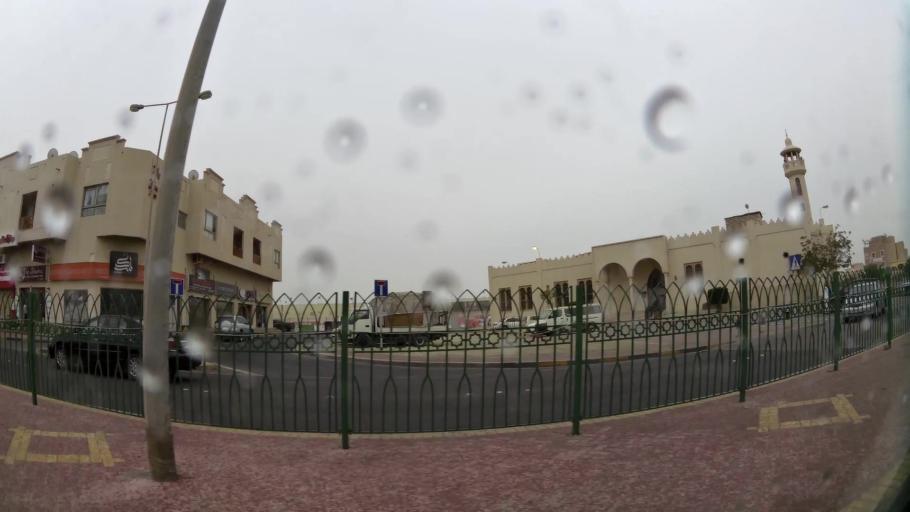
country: BH
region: Northern
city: Madinat `Isa
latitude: 26.1693
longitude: 50.5569
